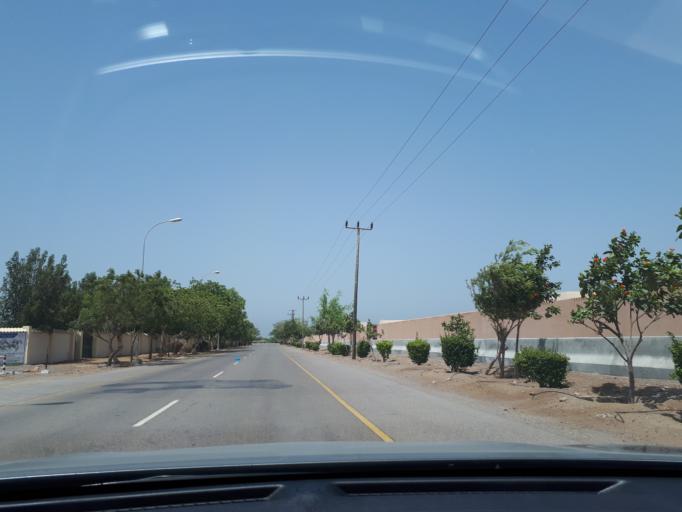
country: OM
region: Muhafazat Masqat
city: As Sib al Jadidah
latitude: 23.6965
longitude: 58.0733
